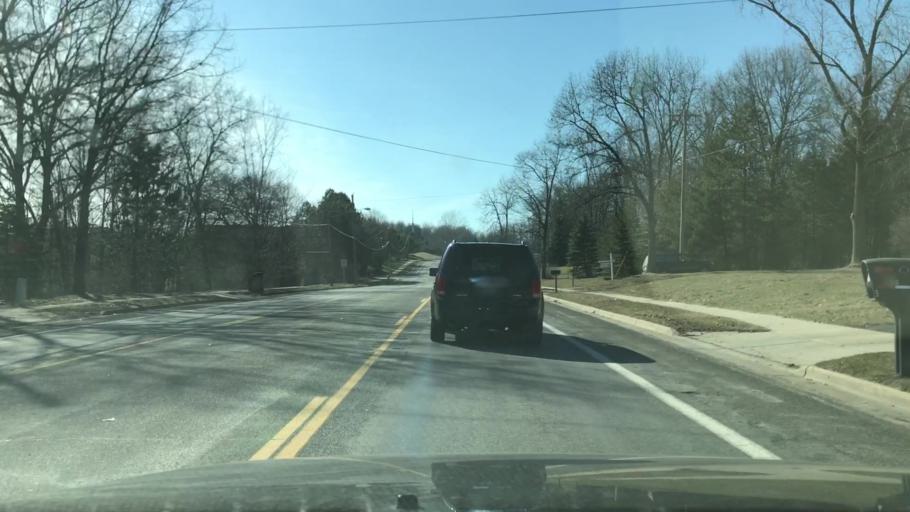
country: US
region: Michigan
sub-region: Kent County
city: East Grand Rapids
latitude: 42.9198
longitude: -85.5529
